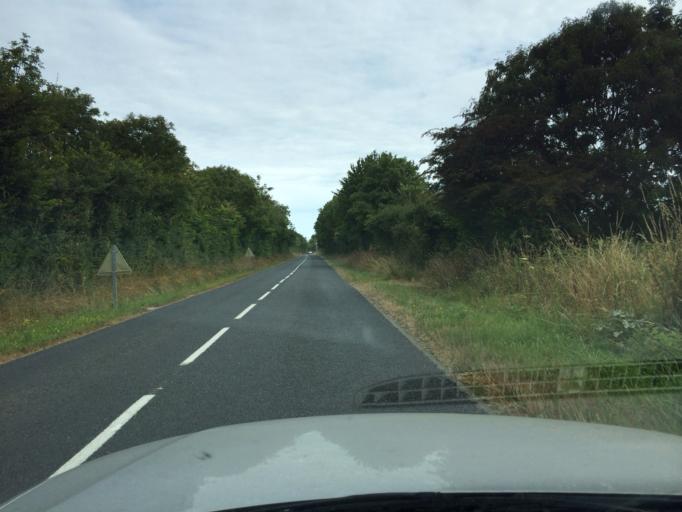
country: FR
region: Lower Normandy
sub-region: Departement de la Manche
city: Sainte-Mere-Eglise
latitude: 49.4439
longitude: -1.2860
